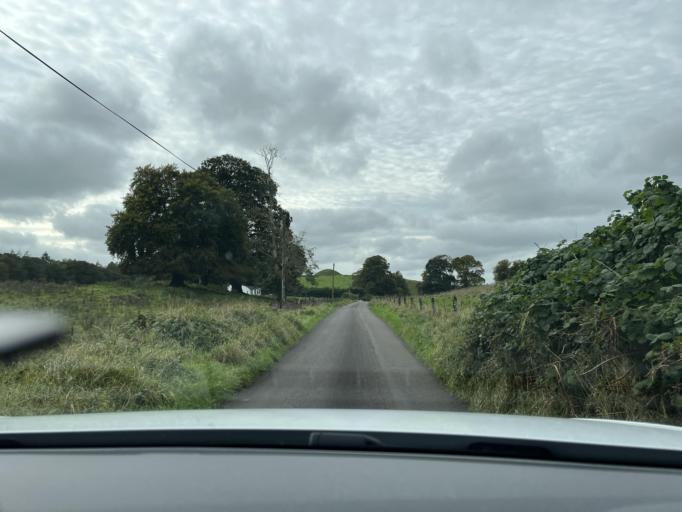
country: IE
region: Connaught
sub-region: Roscommon
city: Boyle
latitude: 53.9724
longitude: -8.2133
